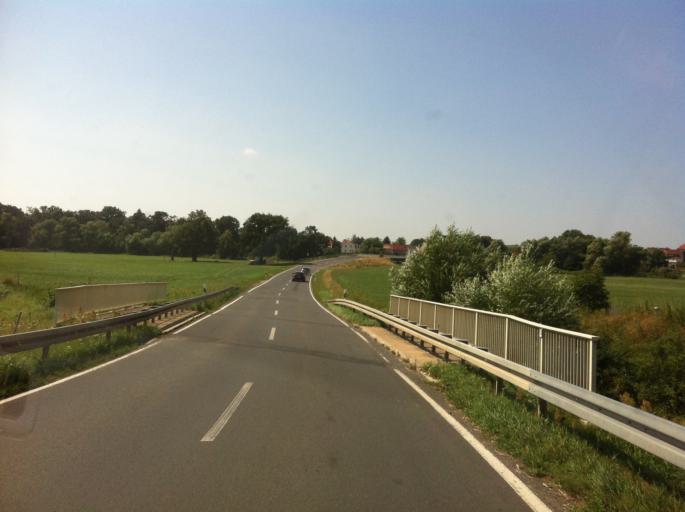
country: DE
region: Saxony
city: Trebsen
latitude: 51.2901
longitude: 12.7639
